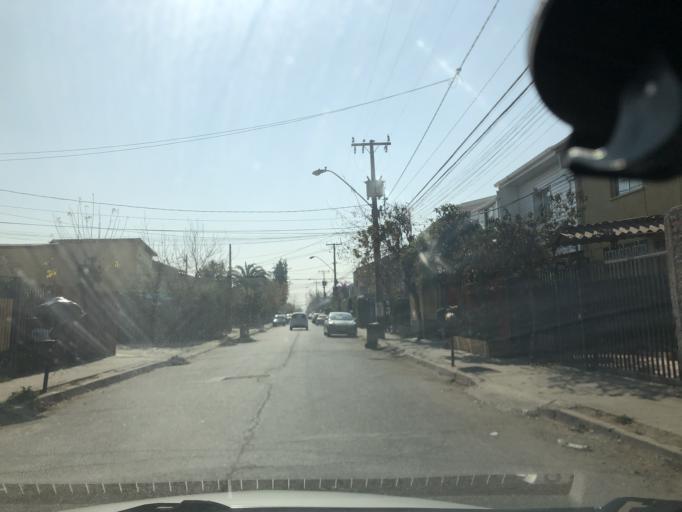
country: CL
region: Santiago Metropolitan
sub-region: Provincia de Cordillera
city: Puente Alto
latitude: -33.5968
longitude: -70.5690
